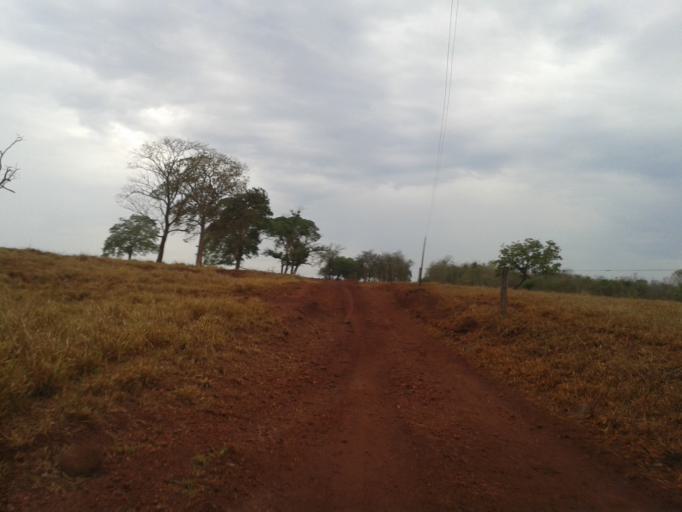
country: BR
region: Minas Gerais
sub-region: Santa Vitoria
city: Santa Vitoria
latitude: -18.8539
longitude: -49.8284
